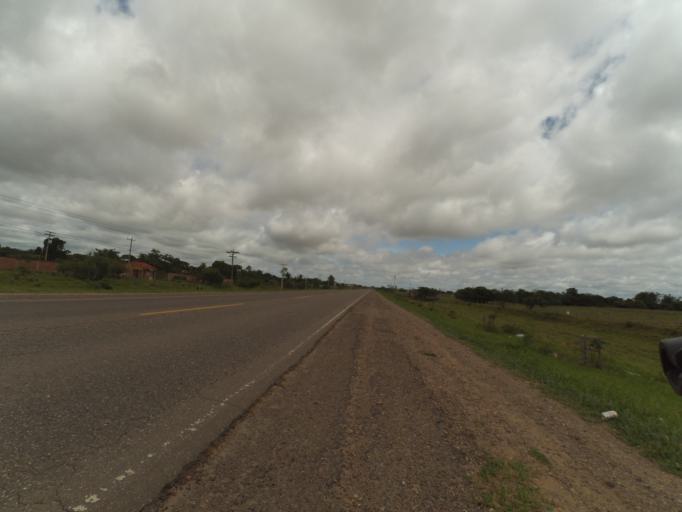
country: BO
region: Santa Cruz
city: Santa Rita
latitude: -17.8903
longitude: -63.2629
